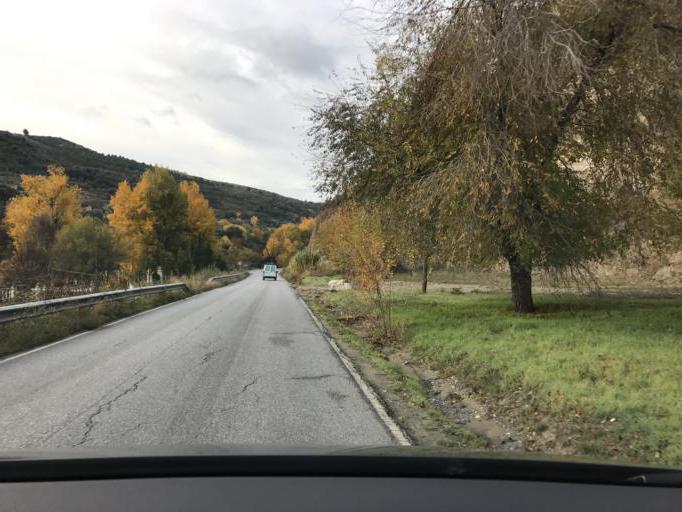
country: ES
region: Andalusia
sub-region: Provincia de Granada
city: Quentar
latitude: 37.1922
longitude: -3.4716
